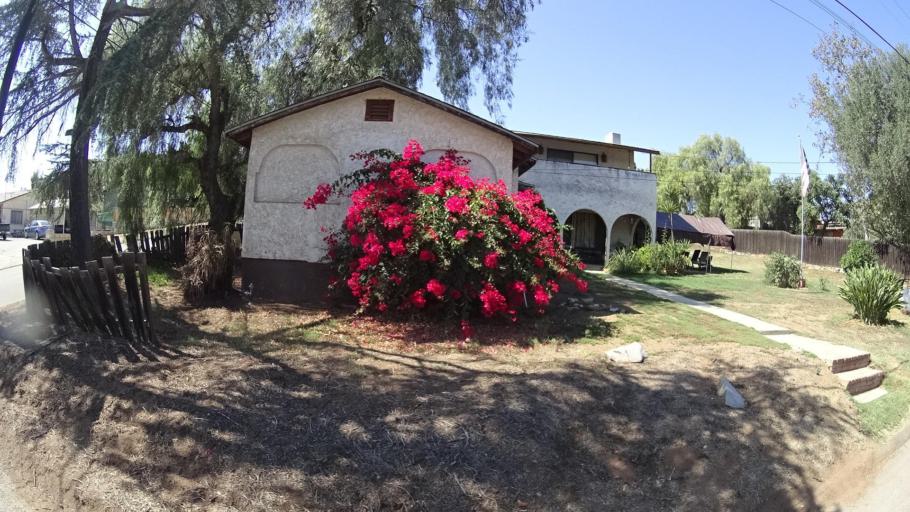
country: US
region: California
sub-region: San Diego County
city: Crest
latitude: 32.8074
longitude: -116.8653
